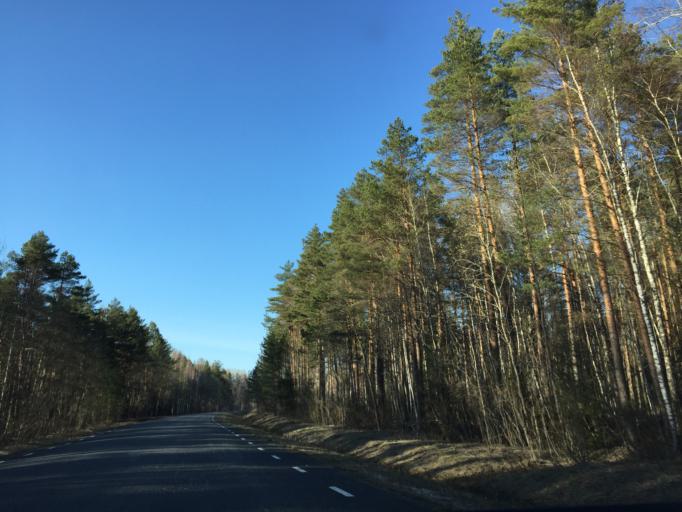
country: RU
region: Pskov
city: Gdov
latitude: 59.0531
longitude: 27.7020
